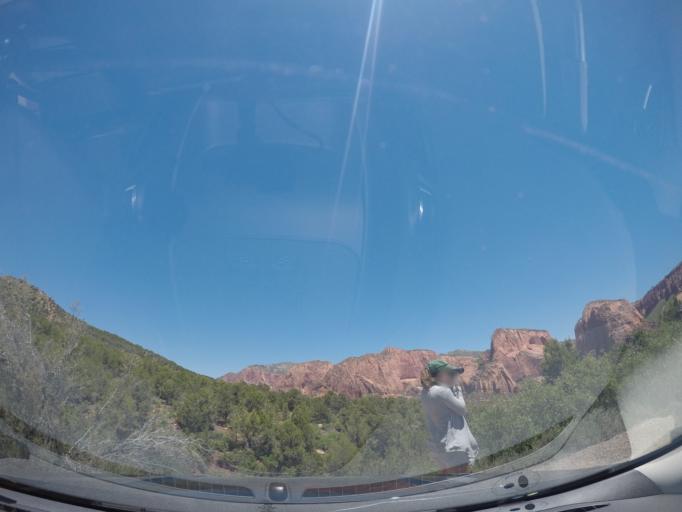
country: US
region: Utah
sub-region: Washington County
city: Toquerville
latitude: 37.4355
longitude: -113.2015
